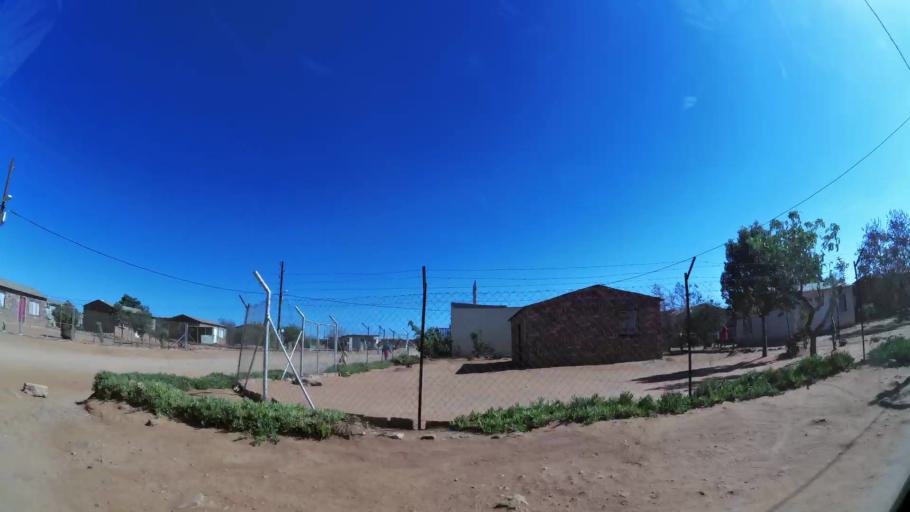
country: ZA
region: Limpopo
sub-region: Capricorn District Municipality
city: Polokwane
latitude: -23.8871
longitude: 29.4064
